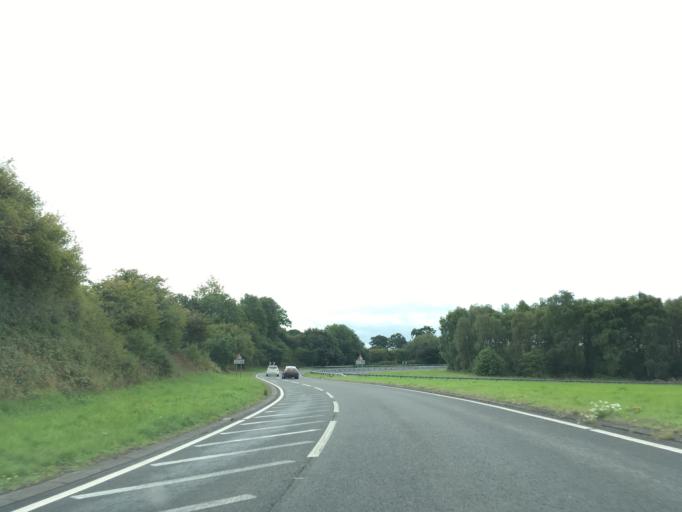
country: GB
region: Wales
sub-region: Monmouthshire
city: Llanarth
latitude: 51.7687
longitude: -2.8319
